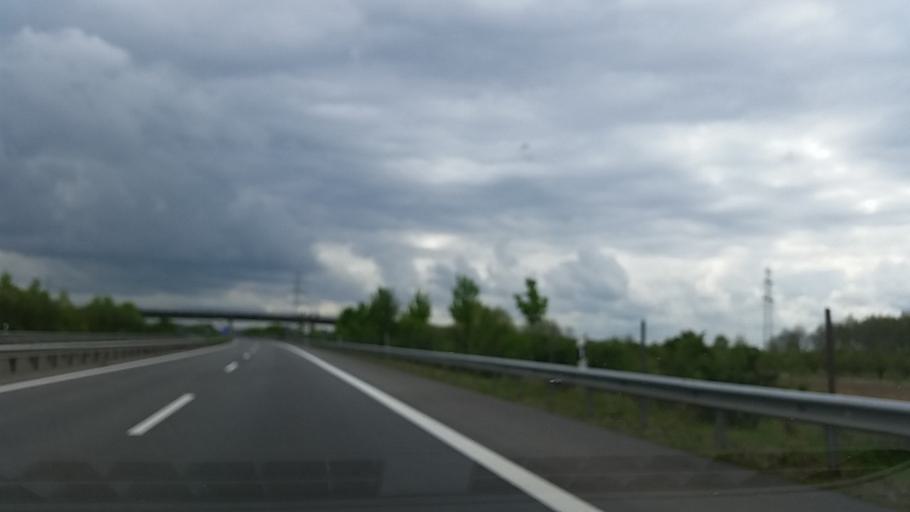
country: DE
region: Lower Saxony
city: Neuenkirchen
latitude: 53.5226
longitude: 9.5834
